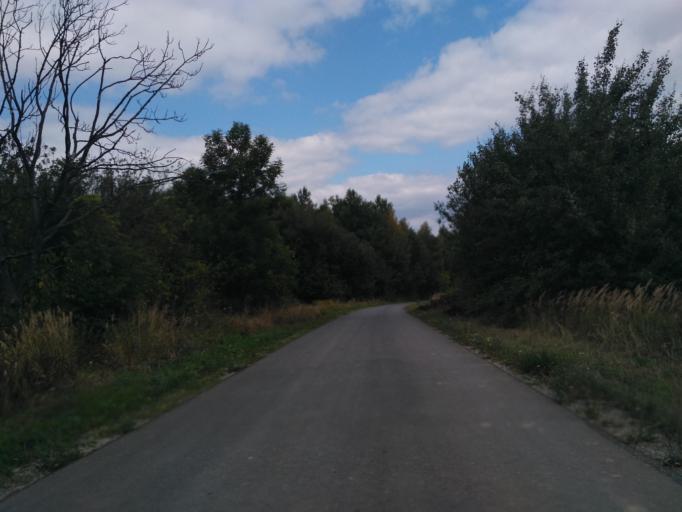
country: PL
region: Subcarpathian Voivodeship
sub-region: Powiat rzeszowski
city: Dynow
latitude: 49.7830
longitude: 22.2800
